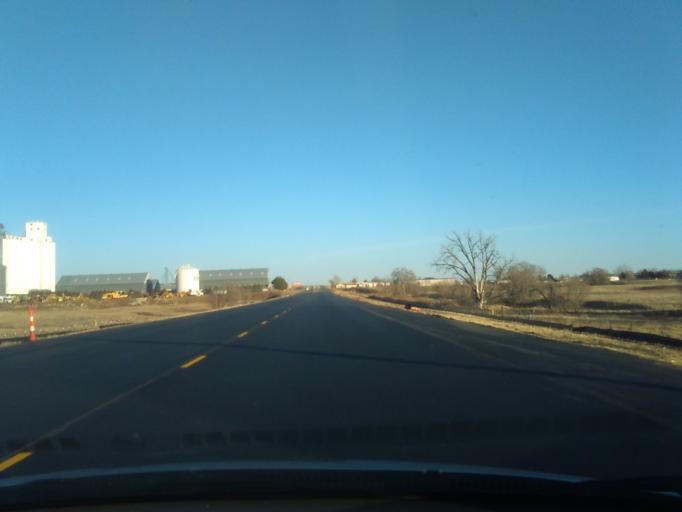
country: US
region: Nebraska
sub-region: Cheyenne County
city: Sidney
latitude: 41.1449
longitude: -102.9608
